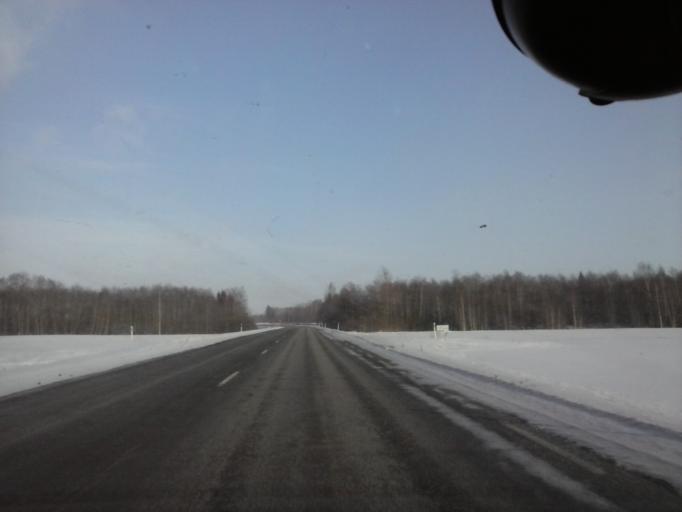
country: EE
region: Tartu
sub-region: Puhja vald
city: Puhja
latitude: 58.3286
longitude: 26.2905
